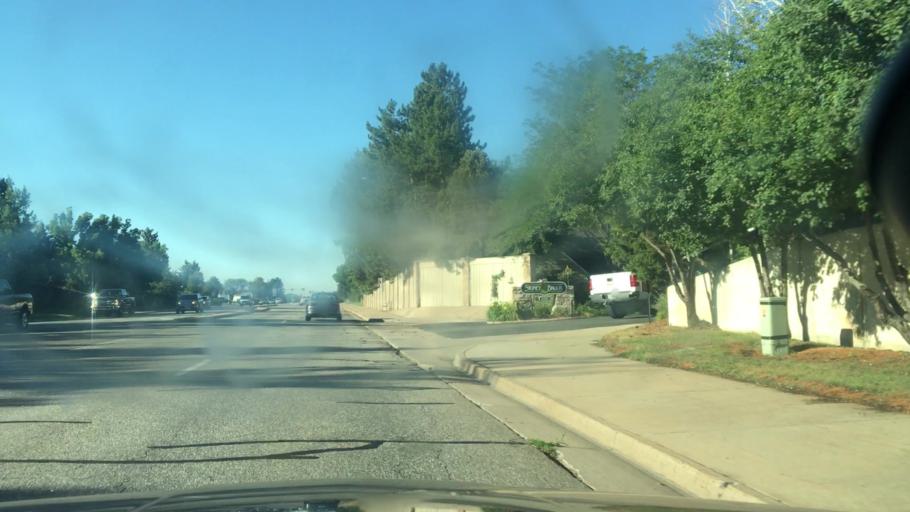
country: US
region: Colorado
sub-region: Arapahoe County
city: Castlewood
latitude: 39.6351
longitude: -104.8853
